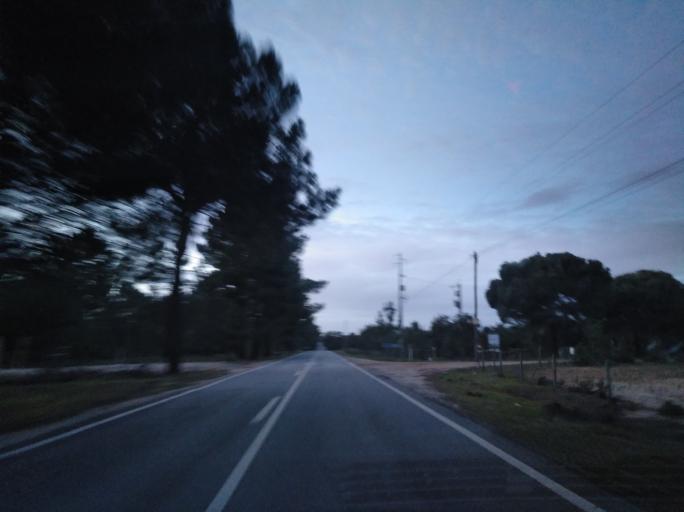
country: PT
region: Setubal
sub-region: Grandola
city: Grandola
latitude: 38.2838
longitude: -8.7080
